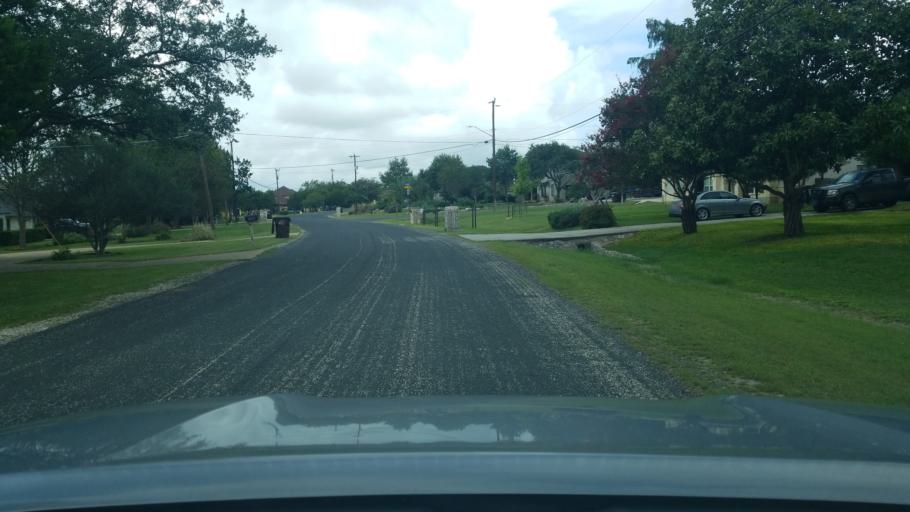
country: US
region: Texas
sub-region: Bexar County
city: Timberwood Park
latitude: 29.6865
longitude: -98.4989
